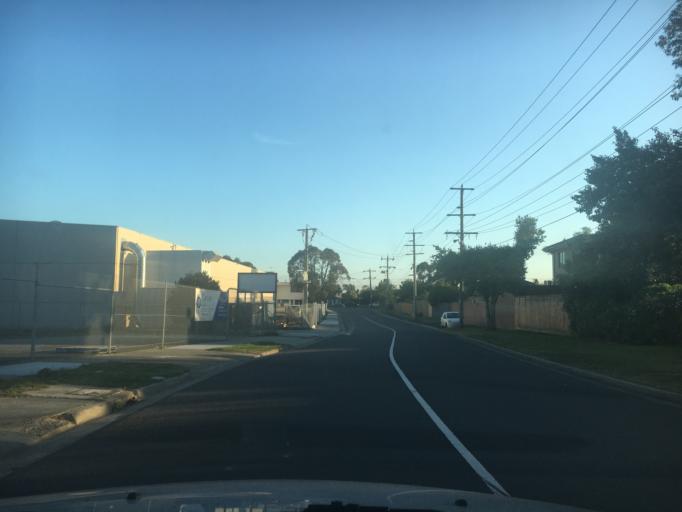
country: AU
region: Victoria
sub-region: Monash
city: Clayton
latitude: -37.9284
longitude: 145.1322
